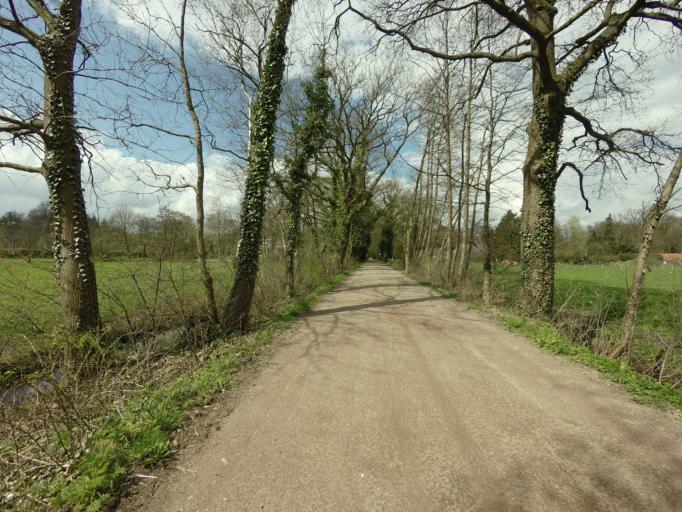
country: NL
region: Utrecht
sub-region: Gemeente Soest
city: Soest
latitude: 52.1696
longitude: 5.2463
